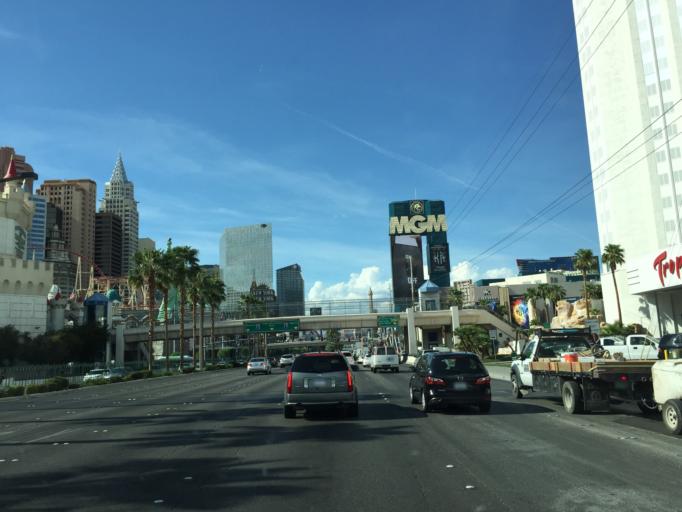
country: US
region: Nevada
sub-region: Clark County
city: Paradise
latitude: 36.0993
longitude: -115.1728
